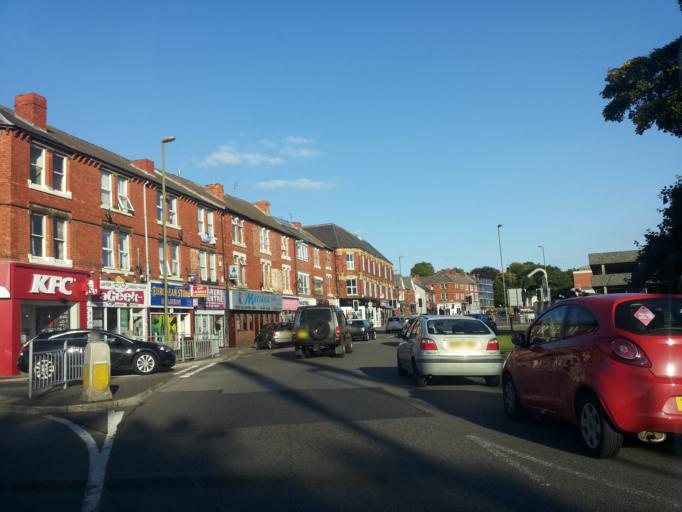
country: GB
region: England
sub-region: Derbyshire
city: Chesterfield
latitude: 53.2357
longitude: -1.4377
